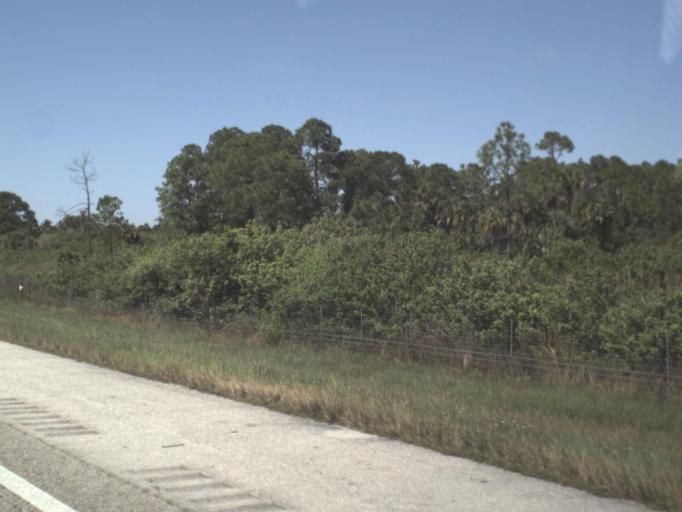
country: US
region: Florida
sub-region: Collier County
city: Orangetree
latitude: 26.1531
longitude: -81.5512
